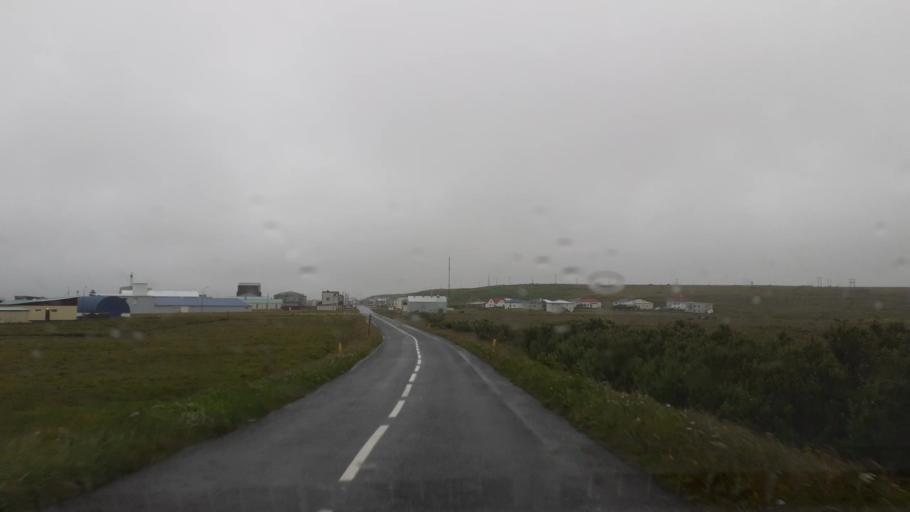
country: IS
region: Northeast
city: Husavik
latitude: 66.4595
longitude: -15.9519
